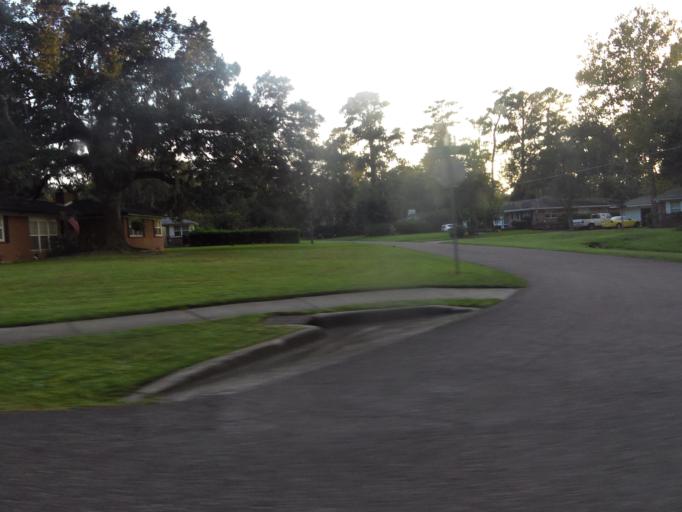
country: US
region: Florida
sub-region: Duval County
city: Jacksonville
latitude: 30.2681
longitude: -81.7122
